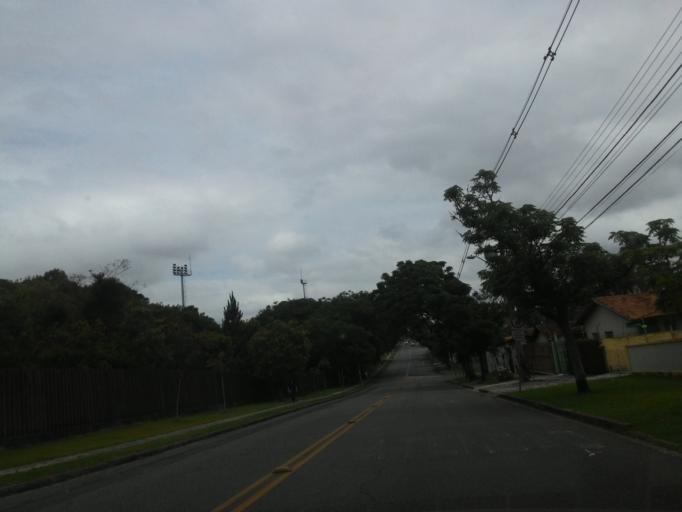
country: BR
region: Parana
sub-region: Curitiba
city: Curitiba
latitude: -25.4554
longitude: -49.2386
